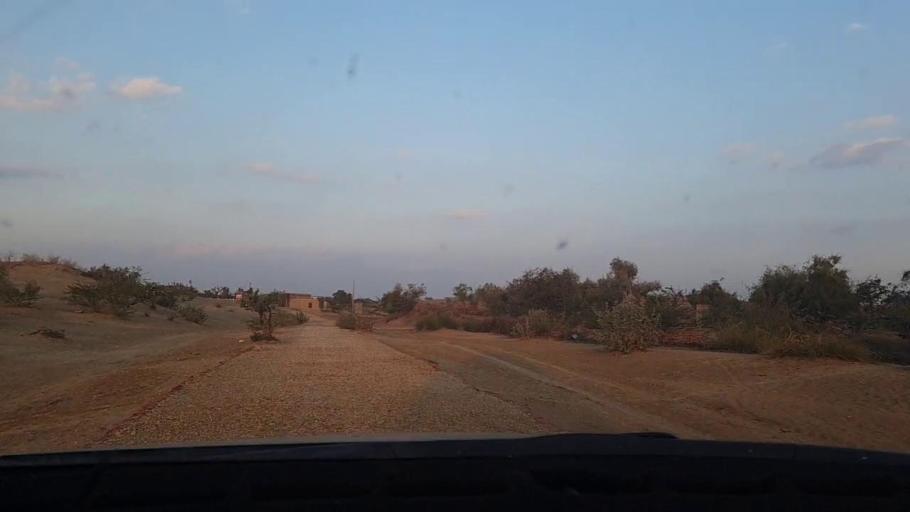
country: PK
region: Sindh
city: Tando Mittha Khan
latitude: 25.9503
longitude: 69.3444
